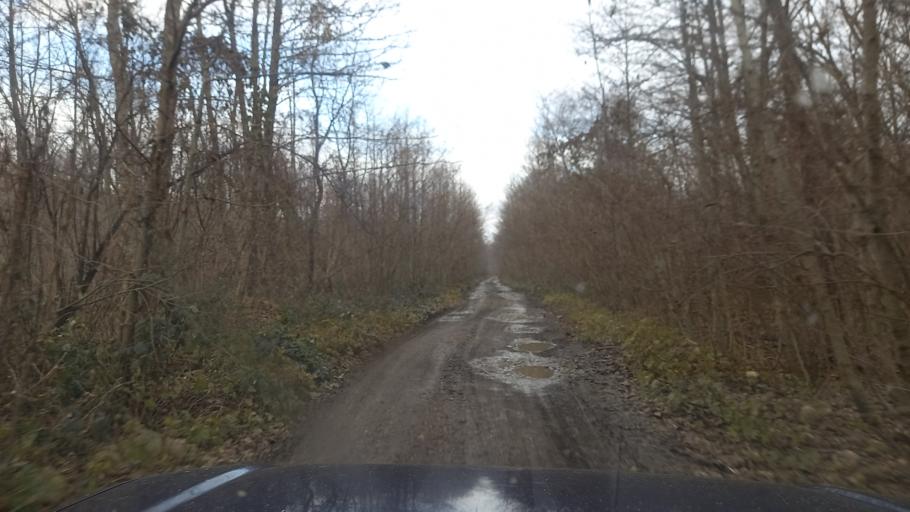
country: RU
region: Krasnodarskiy
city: Neftegorsk
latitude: 44.2210
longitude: 39.7320
